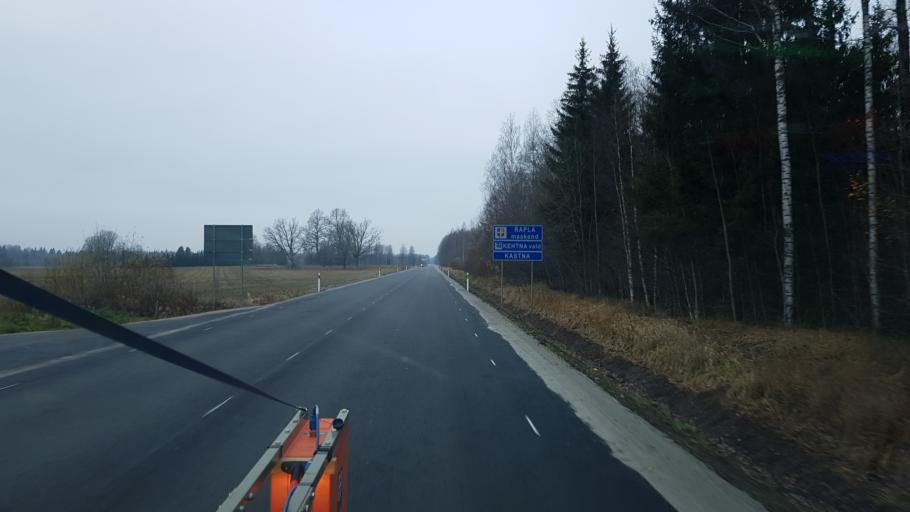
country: EE
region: Paernumaa
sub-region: Vaendra vald (alev)
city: Vandra
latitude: 58.8351
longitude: 25.0866
